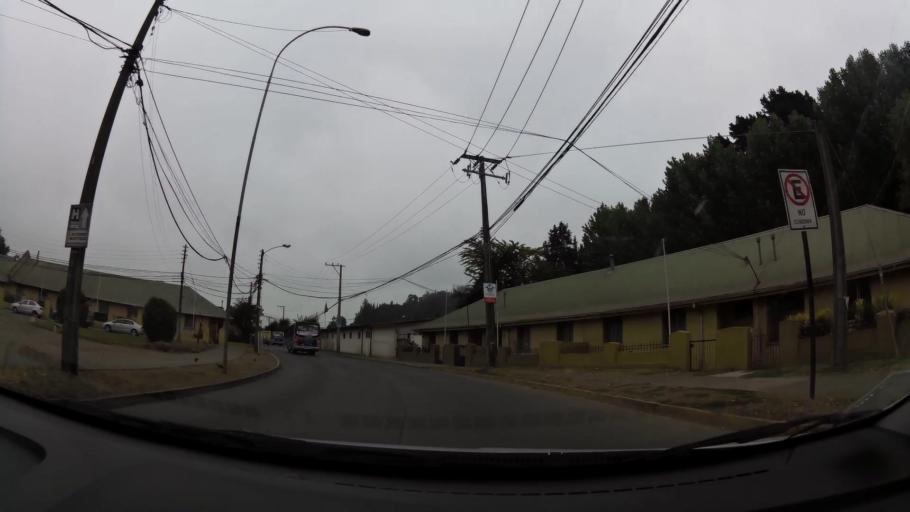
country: CL
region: Biobio
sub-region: Provincia de Concepcion
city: Concepcion
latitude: -36.8157
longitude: -73.0298
